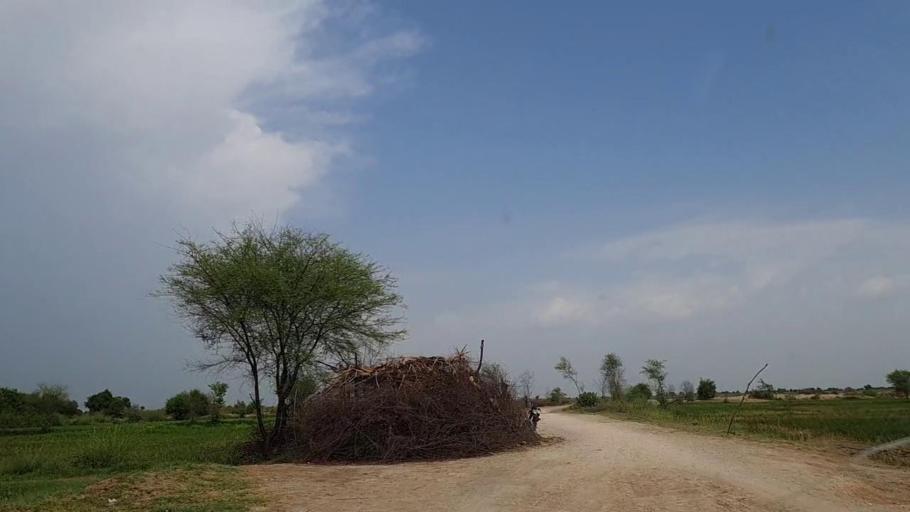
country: PK
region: Sindh
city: Khanpur
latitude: 27.8316
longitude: 69.5059
